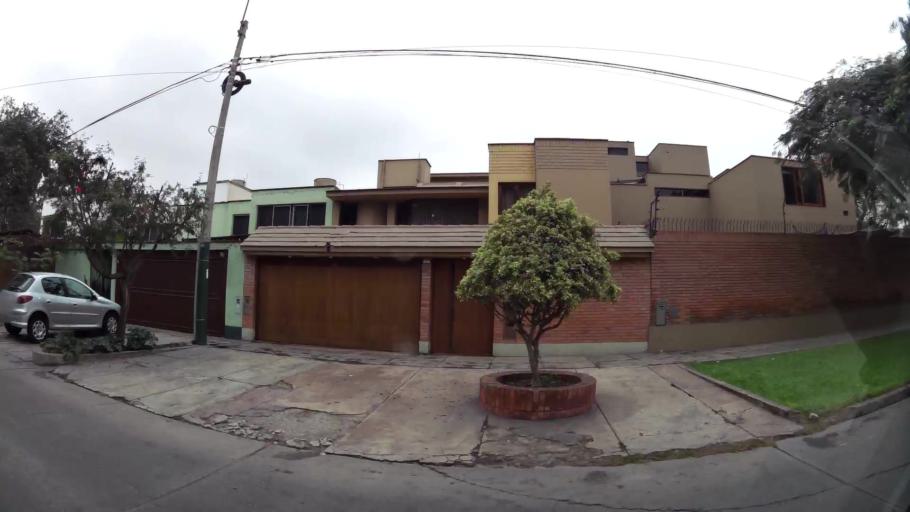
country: PE
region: Lima
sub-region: Lima
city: Surco
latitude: -12.1311
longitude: -77.0060
